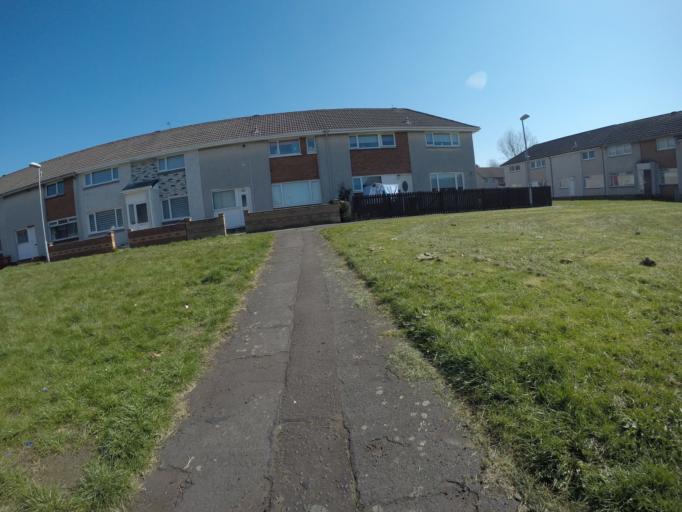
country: GB
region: Scotland
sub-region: North Ayrshire
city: Irvine
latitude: 55.6323
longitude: -4.6600
